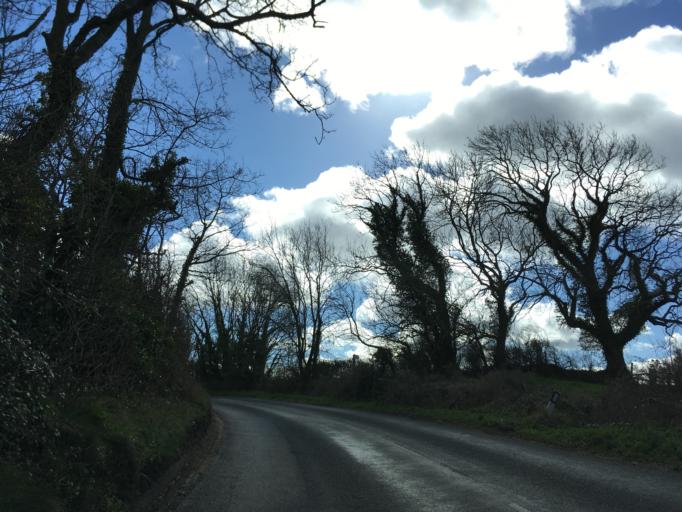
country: GB
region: England
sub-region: South Gloucestershire
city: Horton
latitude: 51.5932
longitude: -2.3348
